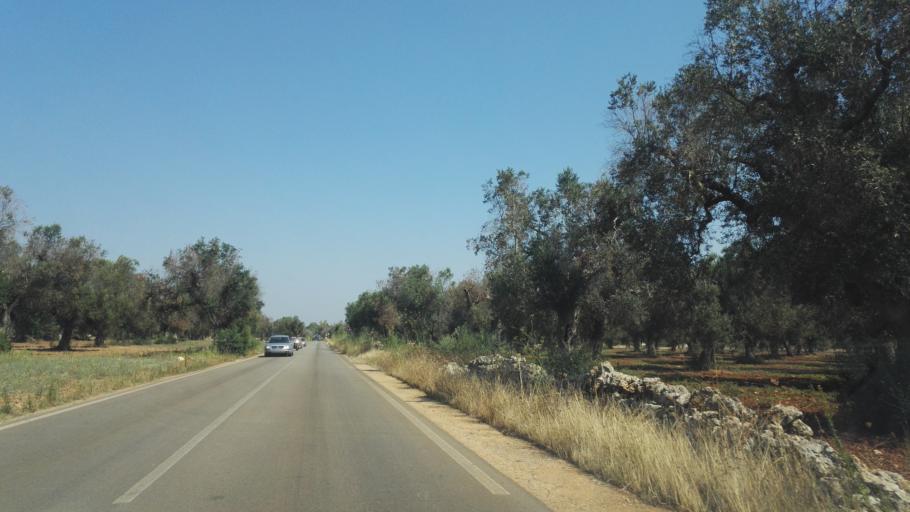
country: IT
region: Apulia
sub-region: Provincia di Lecce
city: Nardo
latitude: 40.1902
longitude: 17.9673
